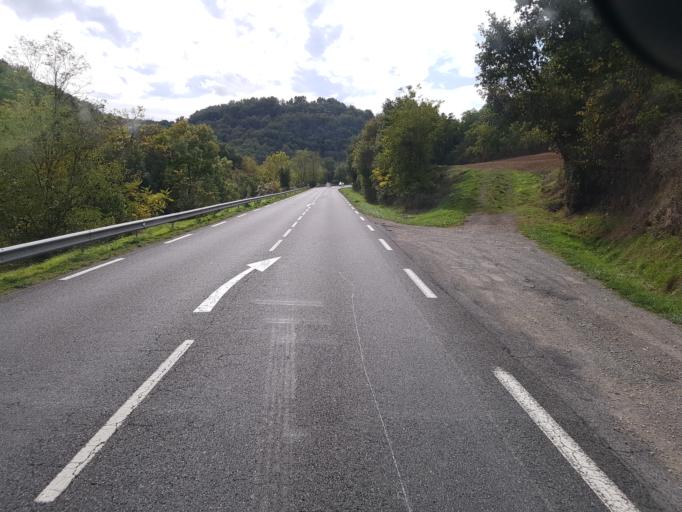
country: FR
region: Midi-Pyrenees
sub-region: Departement de l'Aveyron
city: Saint-Georges-de-Luzencon
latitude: 44.0477
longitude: 2.9769
